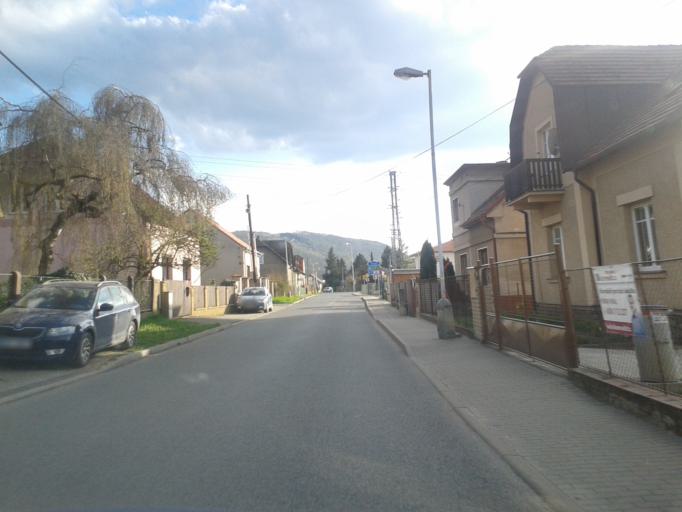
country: CZ
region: Central Bohemia
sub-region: Okres Beroun
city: Kraluv Dvur
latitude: 49.9346
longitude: 14.0258
